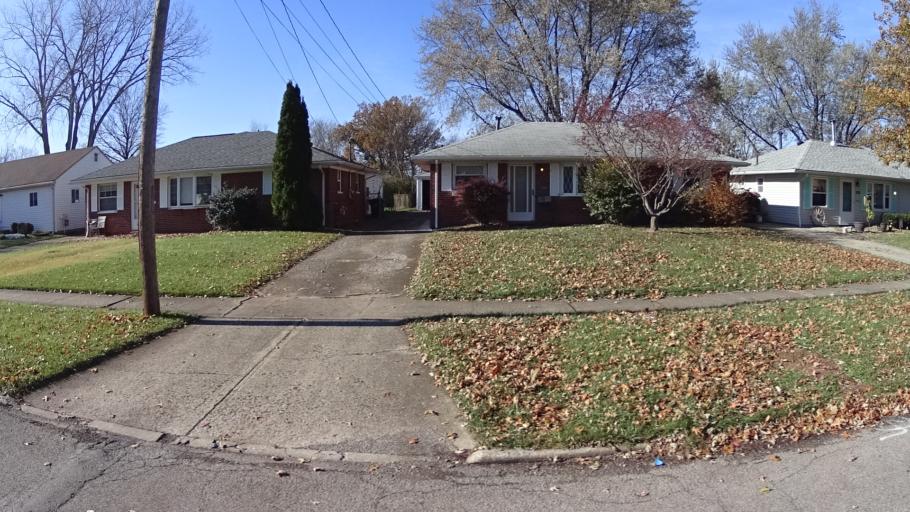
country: US
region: Ohio
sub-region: Lorain County
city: Sheffield Lake
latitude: 41.4952
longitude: -82.0699
